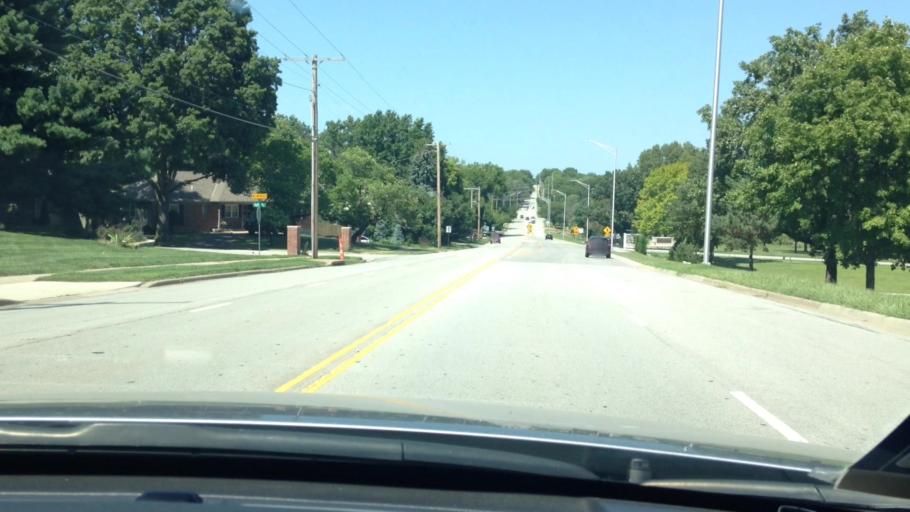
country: US
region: Kansas
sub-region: Johnson County
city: Overland Park
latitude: 38.9586
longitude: -94.6494
